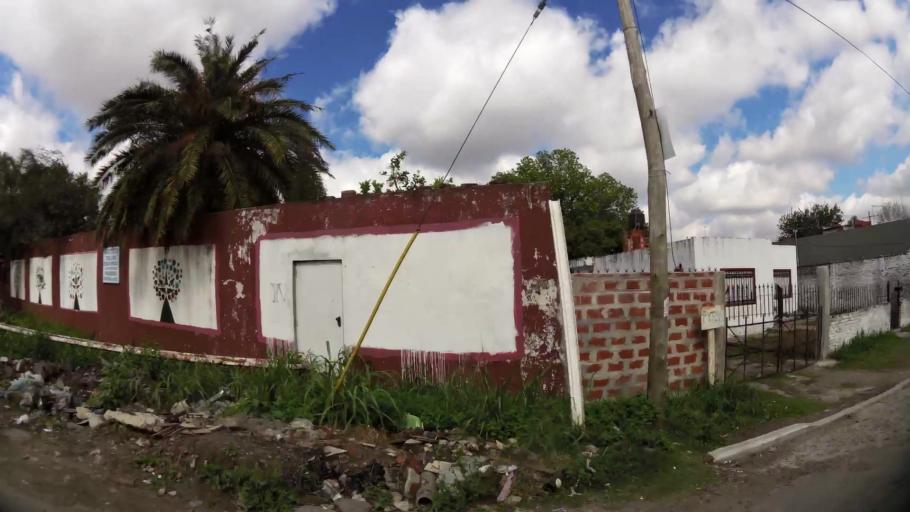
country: AR
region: Buenos Aires
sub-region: Partido de Lanus
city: Lanus
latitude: -34.6896
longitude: -58.4274
